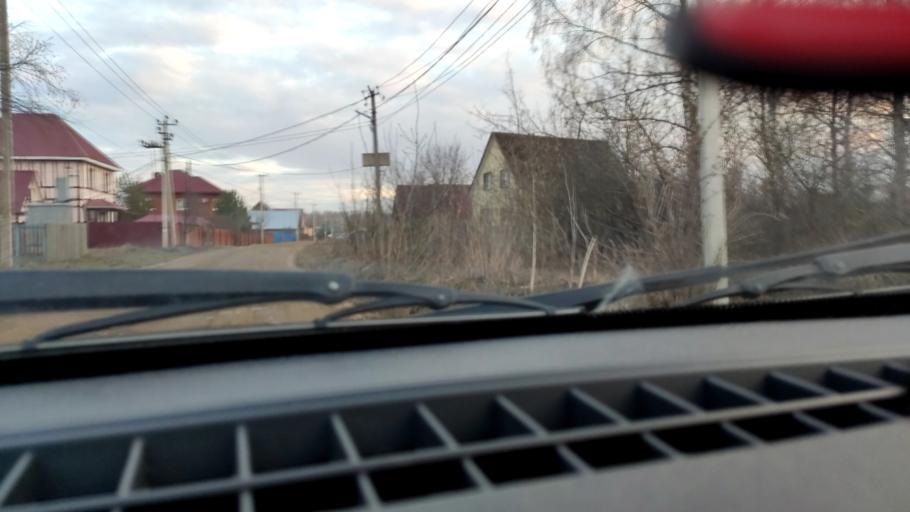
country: RU
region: Bashkortostan
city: Iglino
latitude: 54.8220
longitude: 56.3765
